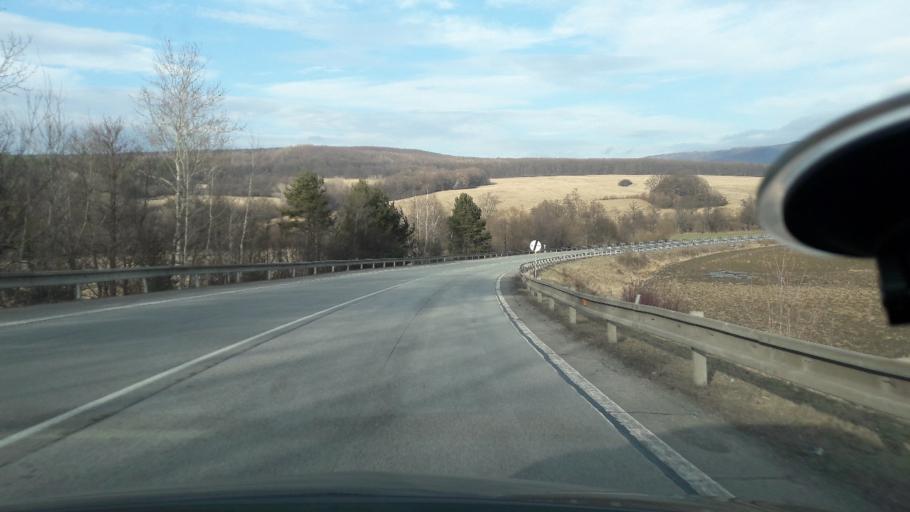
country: SK
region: Nitriansky
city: Prievidza
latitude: 48.7811
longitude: 18.6764
